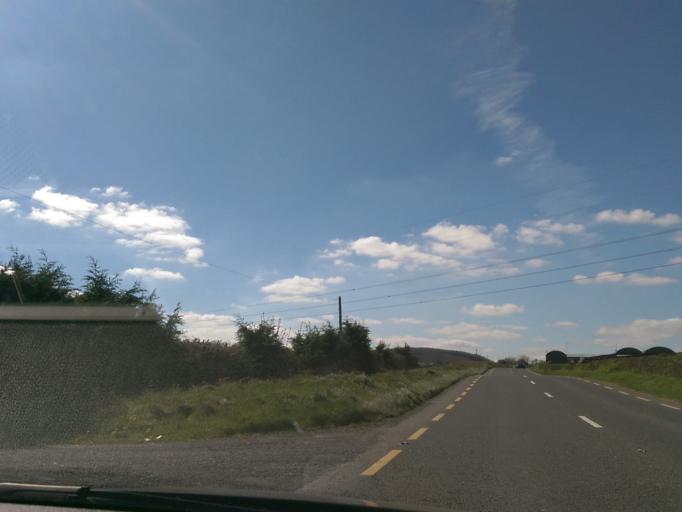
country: IE
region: Leinster
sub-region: Laois
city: Stradbally
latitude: 53.0210
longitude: -7.1680
